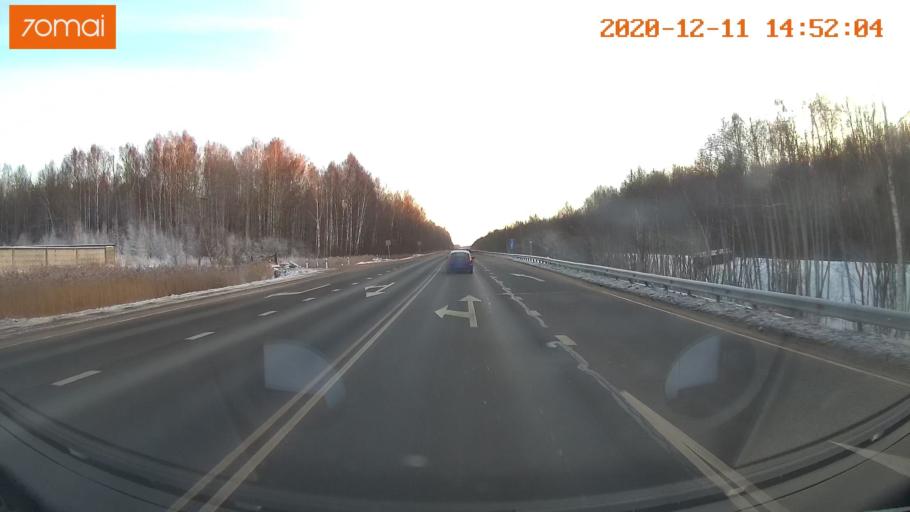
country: RU
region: Kostroma
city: Volgorechensk
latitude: 57.4146
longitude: 41.1961
